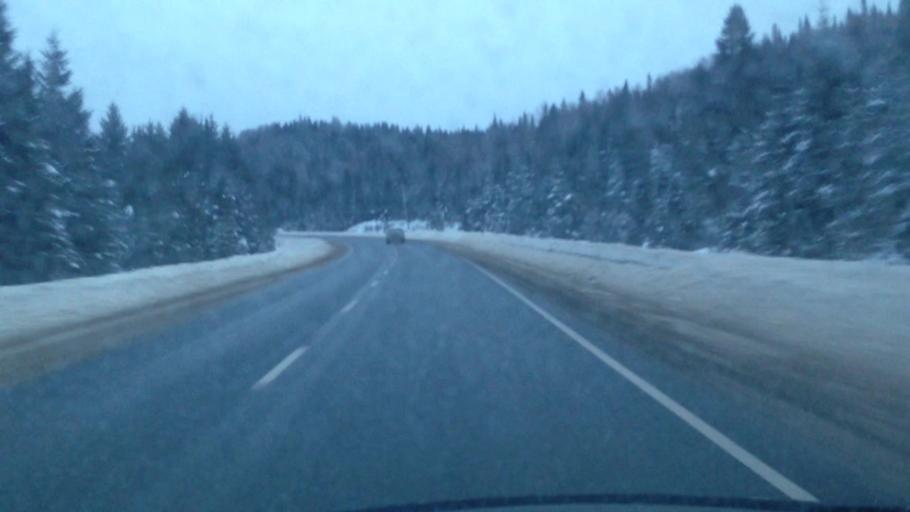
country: CA
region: Quebec
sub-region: Laurentides
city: Sainte-Agathe-des-Monts
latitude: 46.1134
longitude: -74.4273
